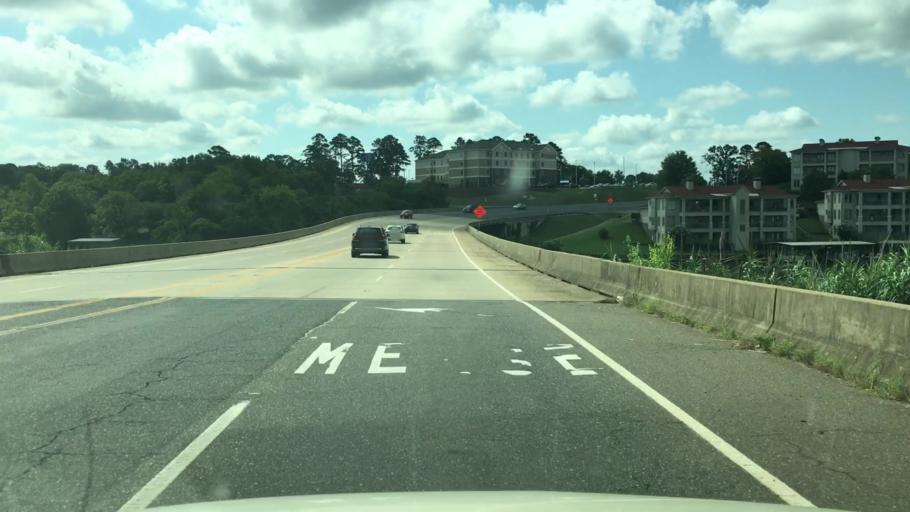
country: US
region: Arkansas
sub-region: Garland County
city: Lake Hamilton
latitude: 34.4308
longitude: -93.0859
